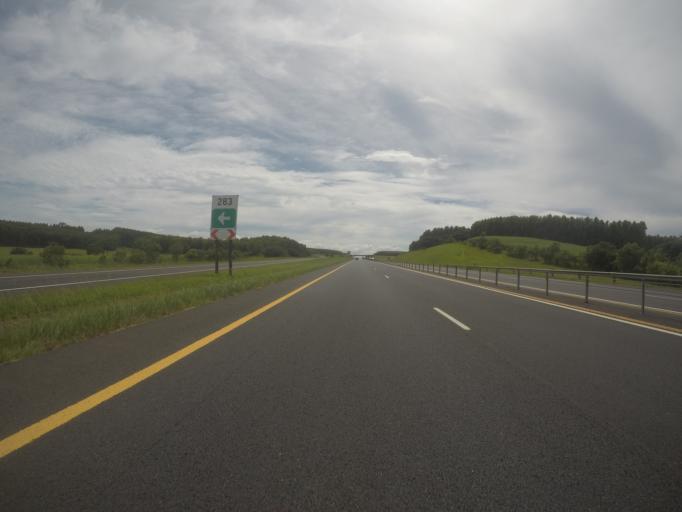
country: ZA
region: KwaZulu-Natal
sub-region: uThungulu District Municipality
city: Eshowe
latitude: -29.0449
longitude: 31.6445
